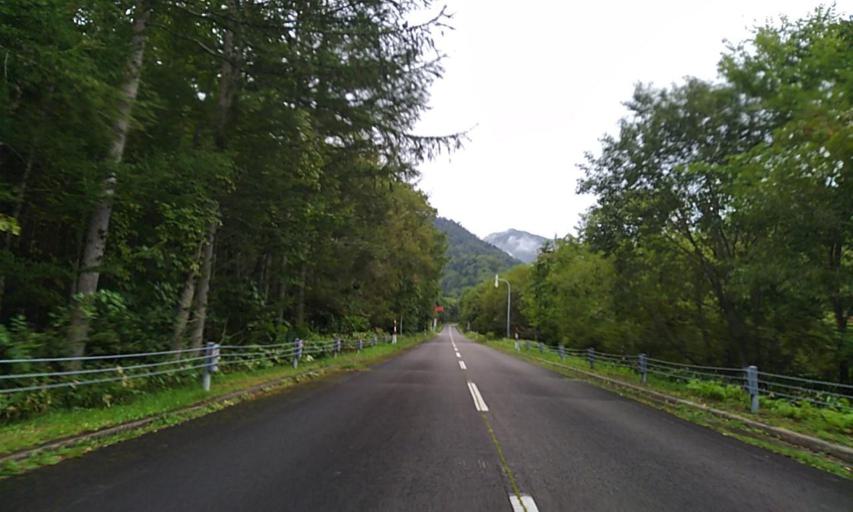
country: JP
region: Hokkaido
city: Bihoro
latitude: 43.5850
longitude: 144.2676
